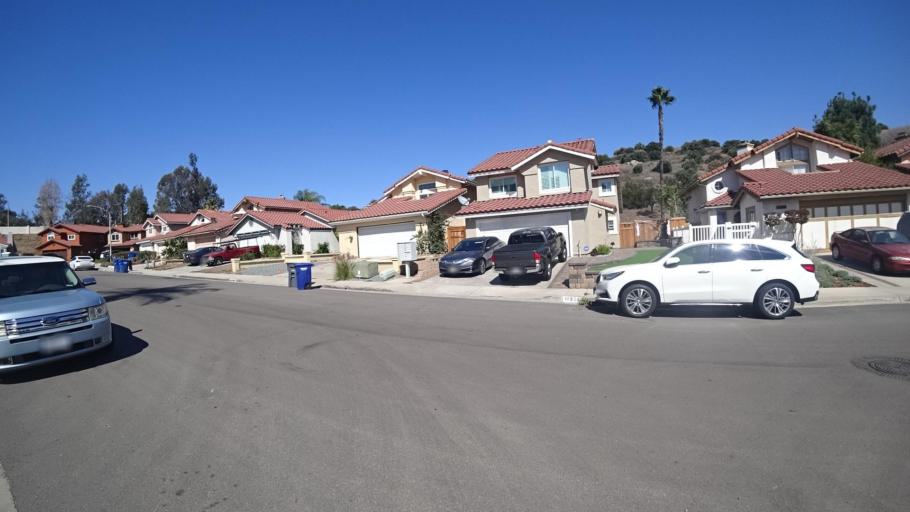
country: US
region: California
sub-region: San Diego County
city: Rancho San Diego
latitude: 32.7510
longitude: -116.9399
